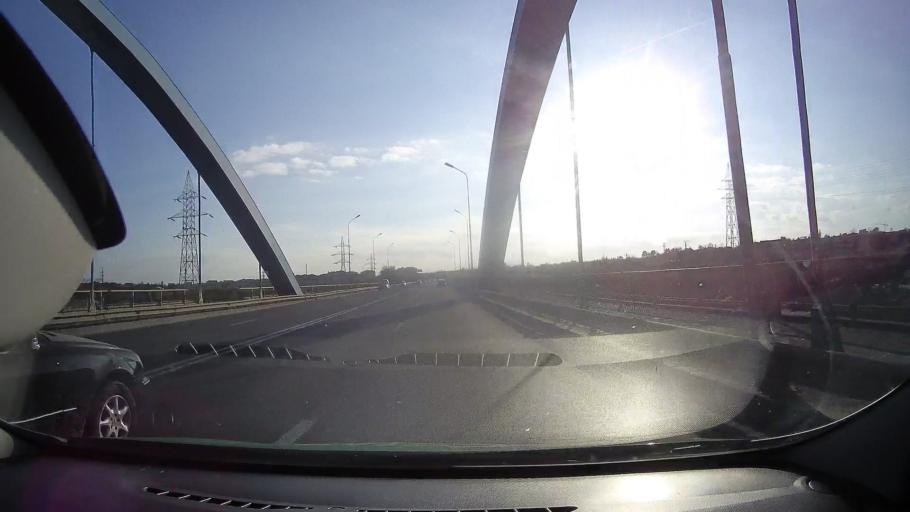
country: RO
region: Constanta
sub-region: Comuna Ovidiu
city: Ovidiu
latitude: 44.2684
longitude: 28.5562
